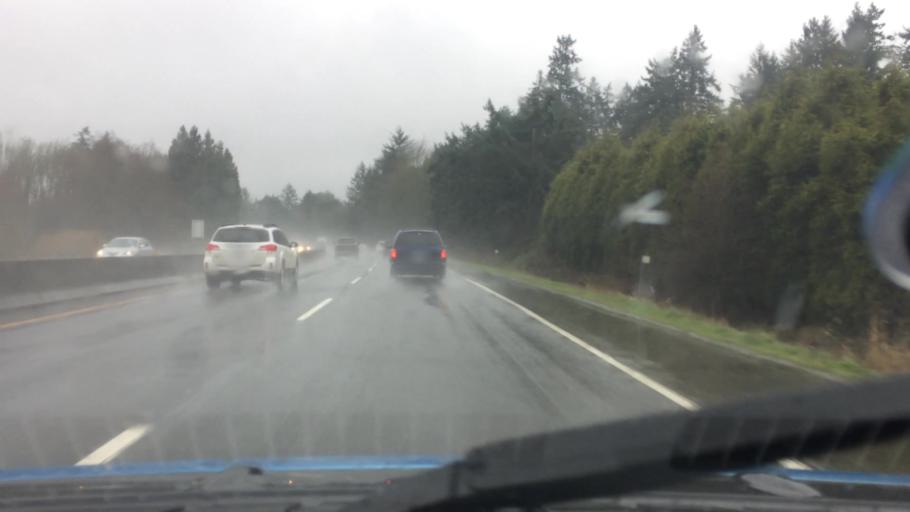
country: CA
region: British Columbia
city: North Saanich
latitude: 48.5695
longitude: -123.3988
